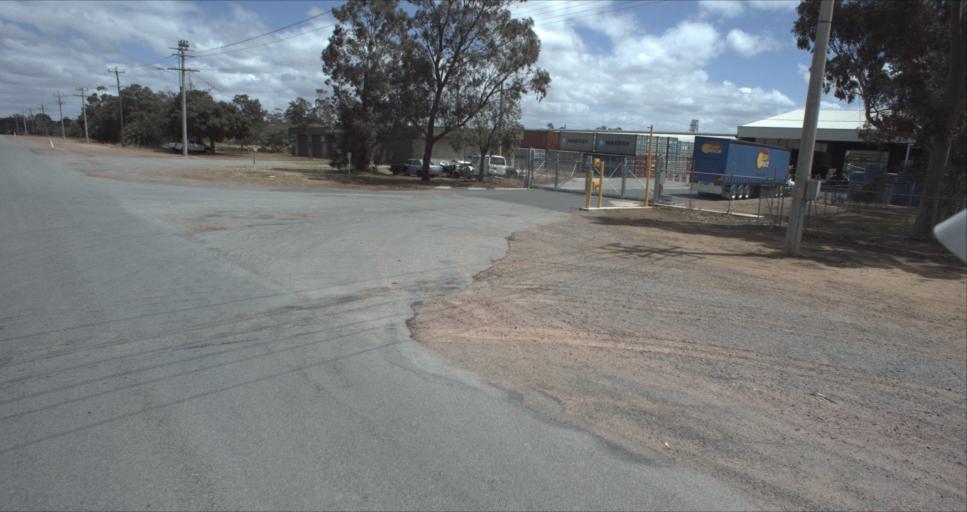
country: AU
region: New South Wales
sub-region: Leeton
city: Leeton
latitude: -34.5580
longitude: 146.3960
